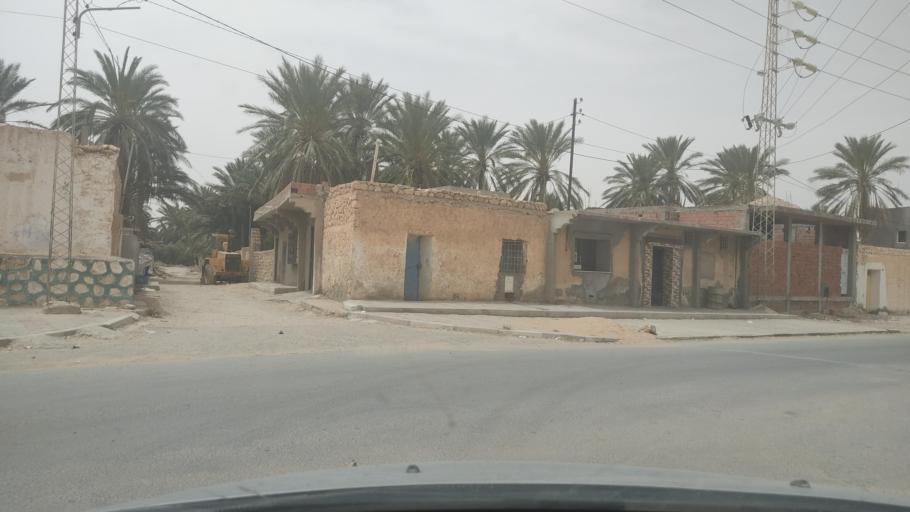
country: TN
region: Gafsa
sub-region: Gafsa Municipality
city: Gafsa
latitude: 34.3314
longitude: 8.9540
